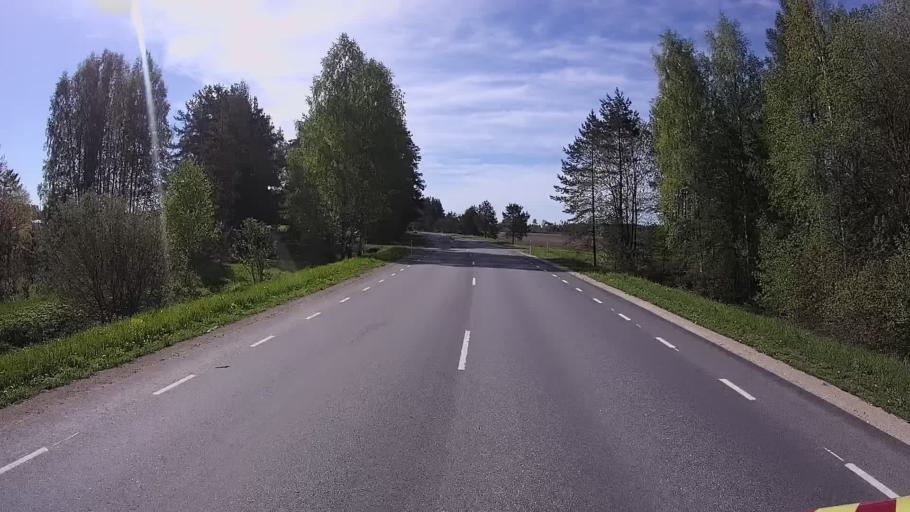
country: EE
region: Tartu
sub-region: UElenurme vald
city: Ulenurme
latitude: 58.3167
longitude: 26.9869
